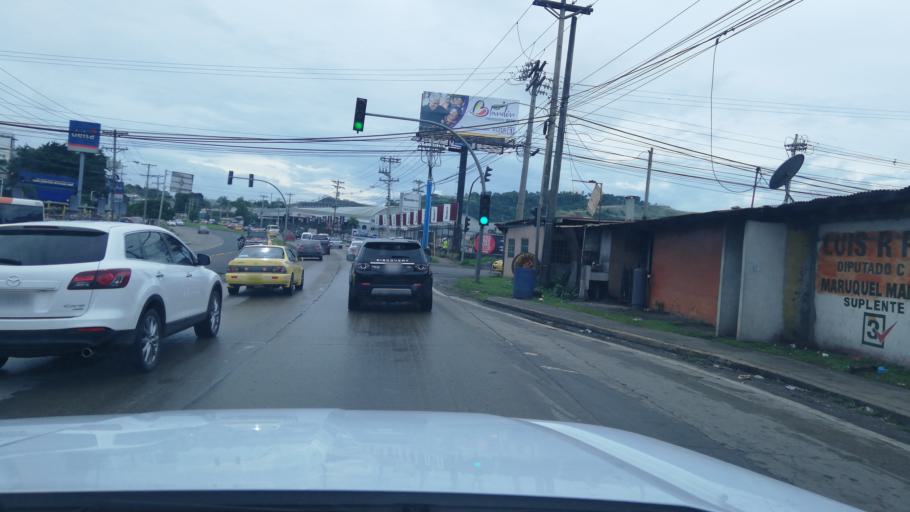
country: PA
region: Panama
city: Las Cumbres
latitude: 9.0725
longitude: -79.5235
